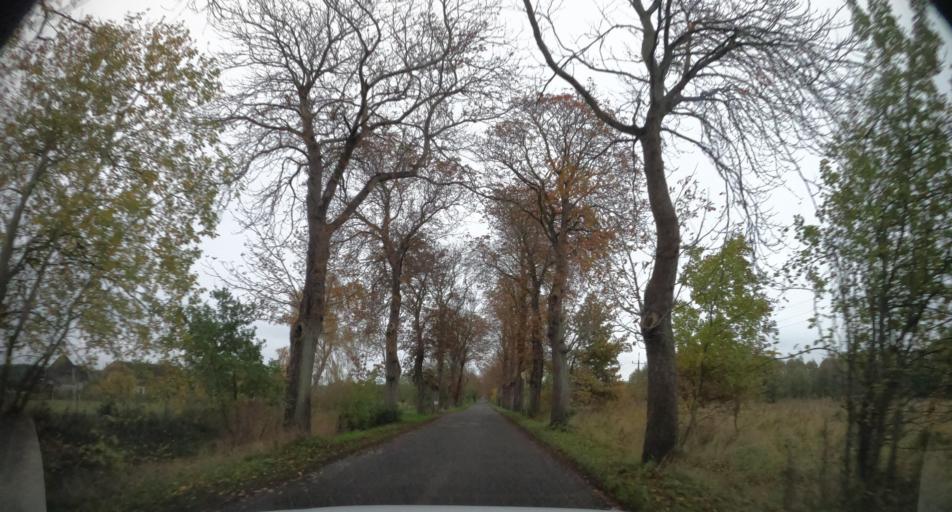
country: PL
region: West Pomeranian Voivodeship
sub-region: Powiat kamienski
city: Wolin
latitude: 53.9299
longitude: 14.6083
